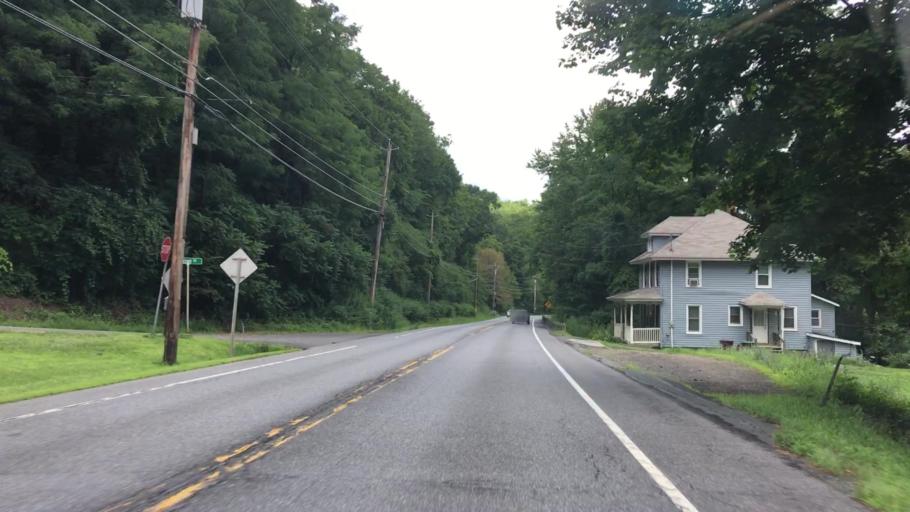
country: US
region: New York
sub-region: Rensselaer County
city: Poestenkill
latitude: 42.8143
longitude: -73.5340
